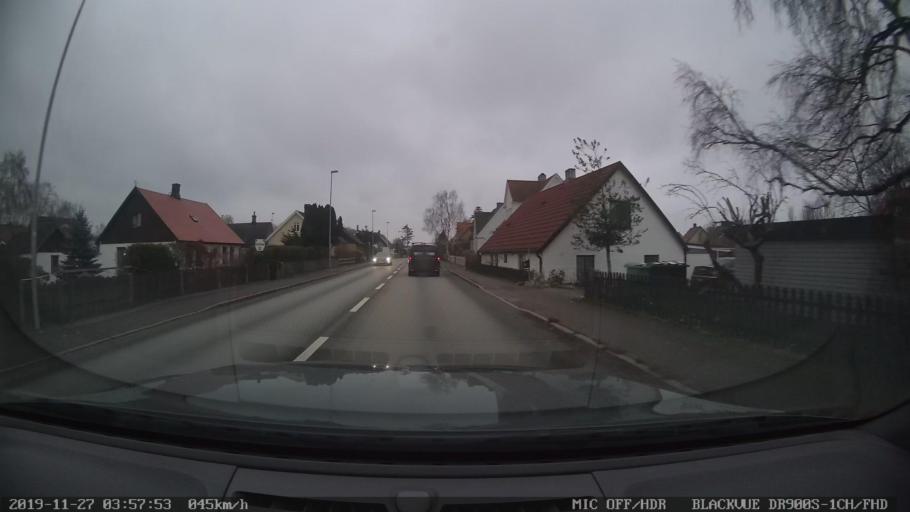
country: SE
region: Skane
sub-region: Hoganas Kommun
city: Hoganas
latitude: 56.2095
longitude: 12.5550
